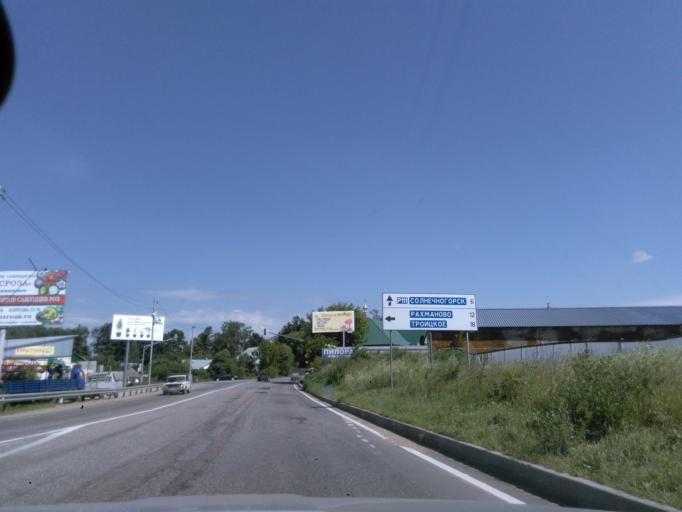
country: RU
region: Moskovskaya
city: Solnechnogorsk
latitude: 56.1457
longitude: 36.9168
